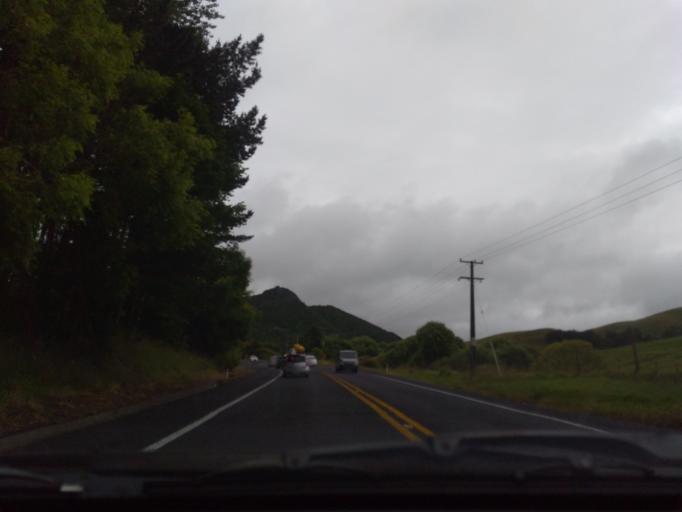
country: NZ
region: Auckland
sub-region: Auckland
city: Wellsford
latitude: -36.1239
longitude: 174.4339
